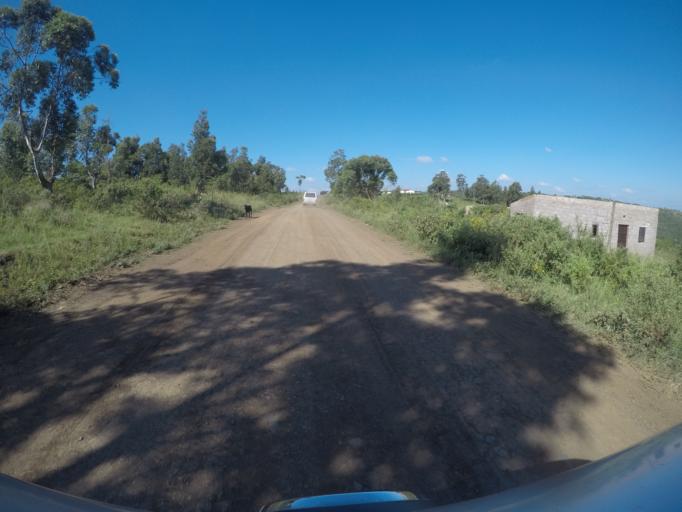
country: ZA
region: KwaZulu-Natal
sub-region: uThungulu District Municipality
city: Empangeni
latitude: -28.5647
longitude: 31.6996
